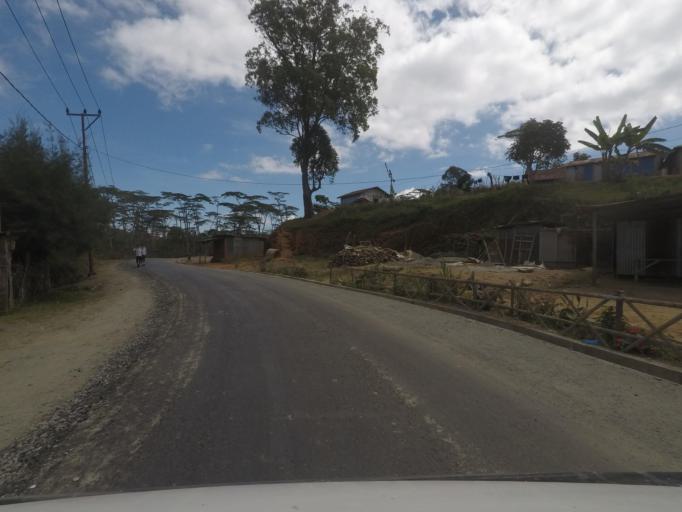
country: TL
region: Ermera
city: Gleno
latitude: -8.7499
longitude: 125.3531
